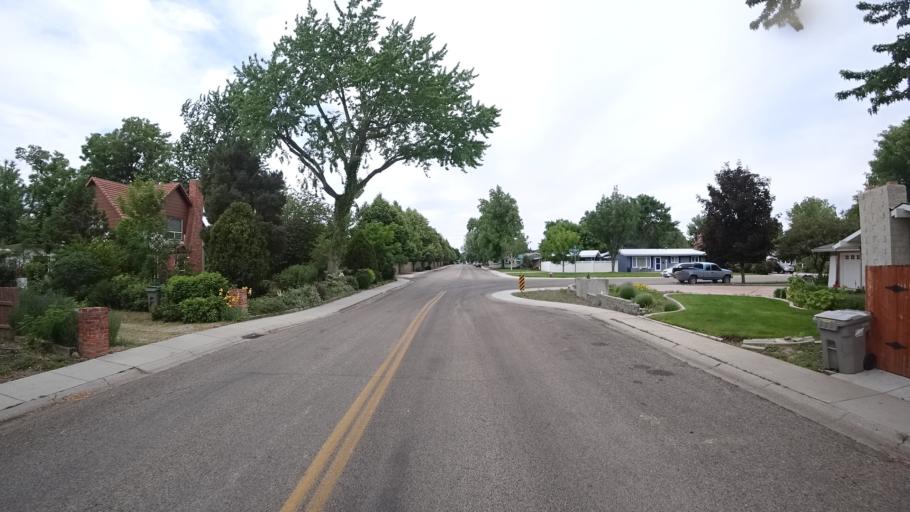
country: US
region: Idaho
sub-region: Ada County
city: Boise
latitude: 43.5772
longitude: -116.2082
